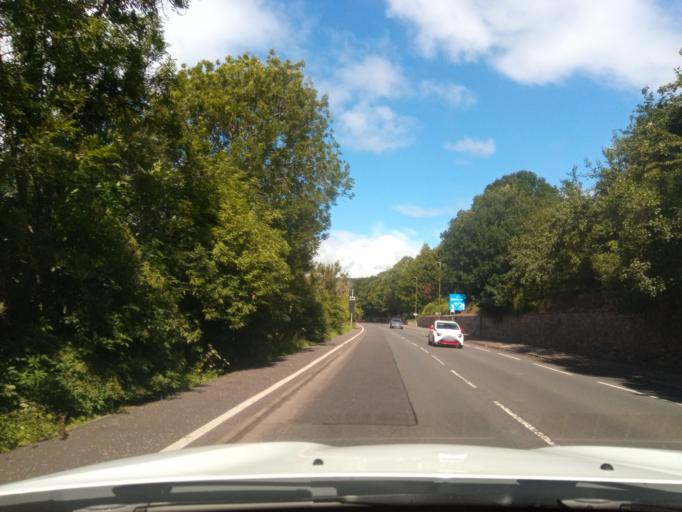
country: GB
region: Scotland
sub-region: Stirling
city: Bridge of Allan
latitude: 56.1422
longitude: -3.9266
